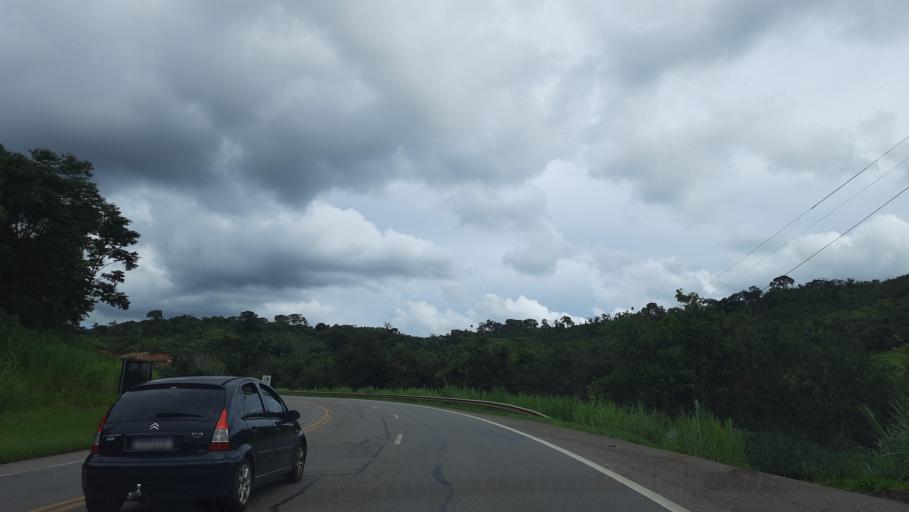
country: BR
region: Sao Paulo
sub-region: Sao Joao Da Boa Vista
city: Sao Joao da Boa Vista
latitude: -21.9366
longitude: -46.7055
